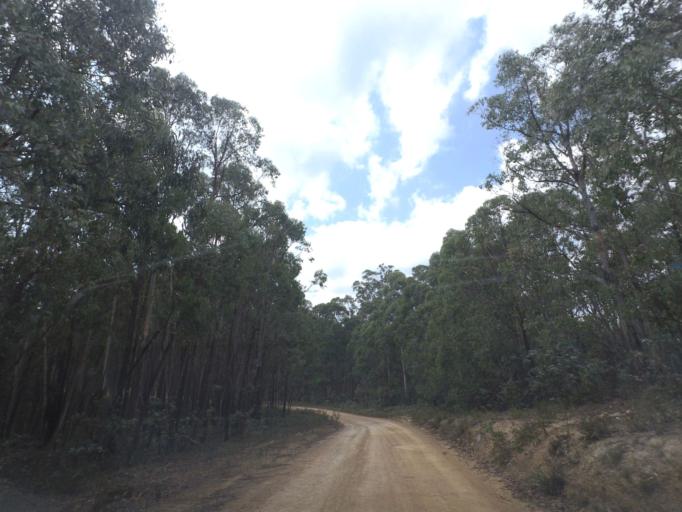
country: AU
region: Victoria
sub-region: Moorabool
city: Bacchus Marsh
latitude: -37.4680
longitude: 144.3930
